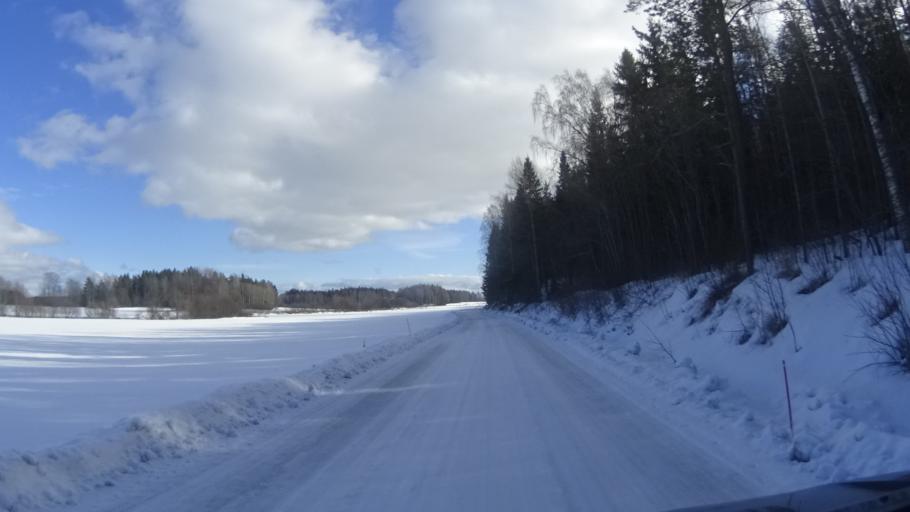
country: FI
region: Uusimaa
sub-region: Helsinki
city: Vantaa
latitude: 60.2471
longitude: 25.1711
